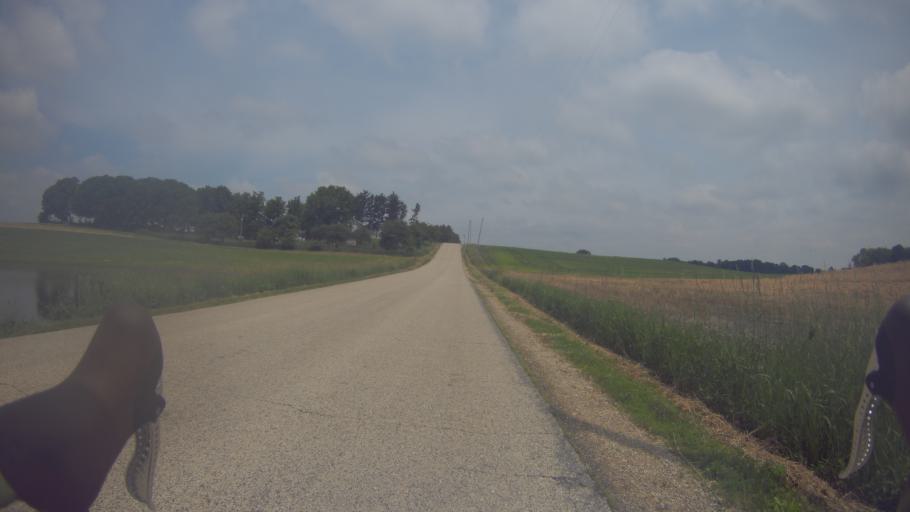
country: US
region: Wisconsin
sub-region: Jefferson County
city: Lake Ripley
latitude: 42.9818
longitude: -88.9985
